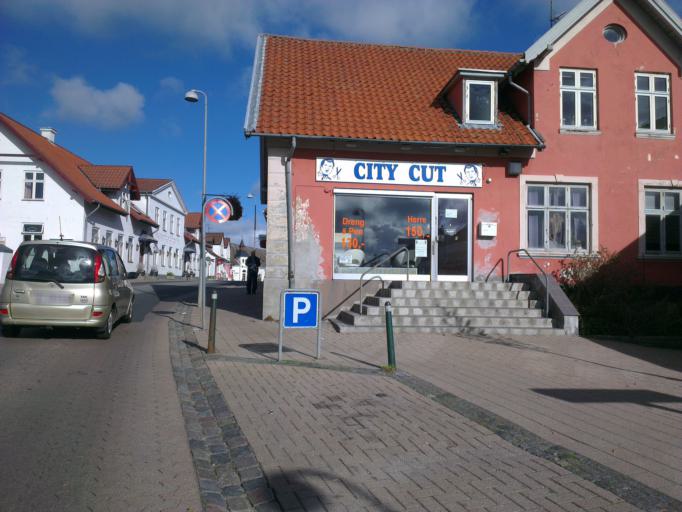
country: DK
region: Capital Region
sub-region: Frederikssund Kommune
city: Slangerup
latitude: 55.8456
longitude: 12.1719
